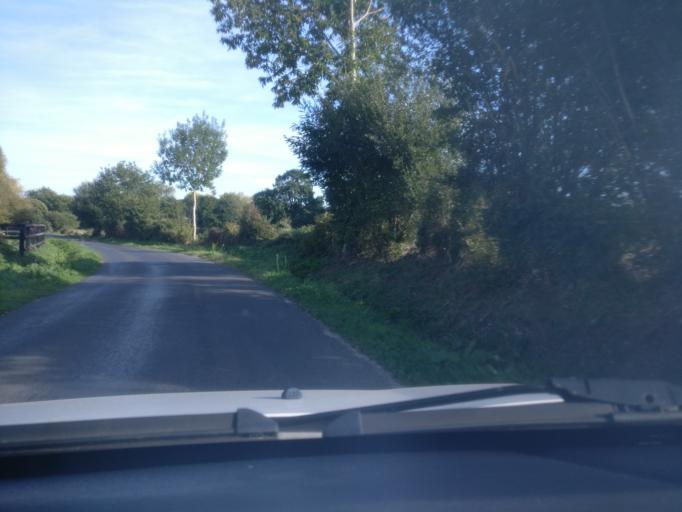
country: FR
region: Lower Normandy
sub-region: Departement de la Manche
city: Sartilly
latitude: 48.7071
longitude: -1.4631
